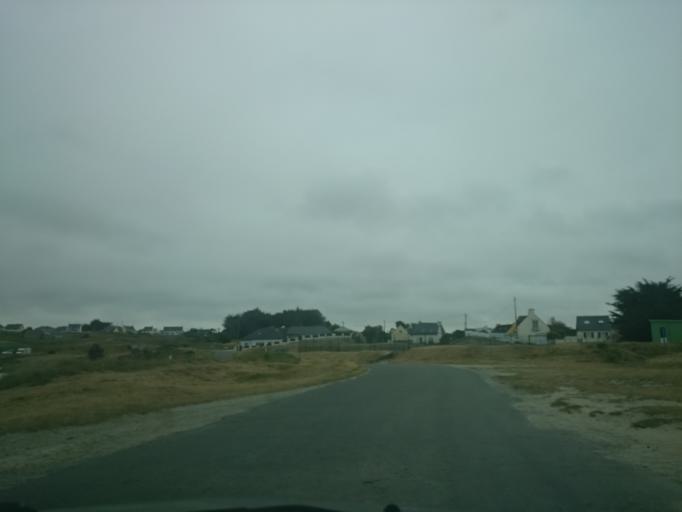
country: FR
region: Brittany
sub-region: Departement du Finistere
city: Saint-Pabu
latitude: 48.5763
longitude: -4.6266
